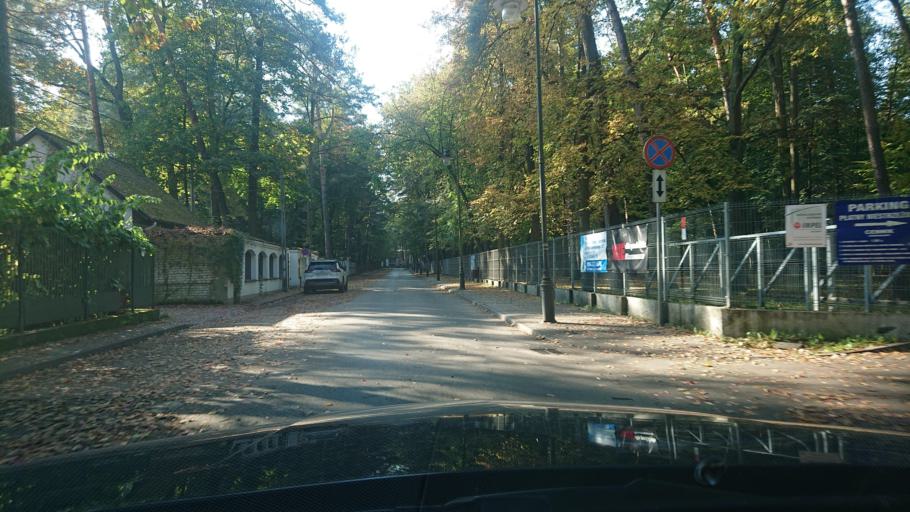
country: PL
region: Masovian Voivodeship
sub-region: Powiat piaseczynski
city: Konstancin-Jeziorna
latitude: 52.0817
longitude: 21.1140
